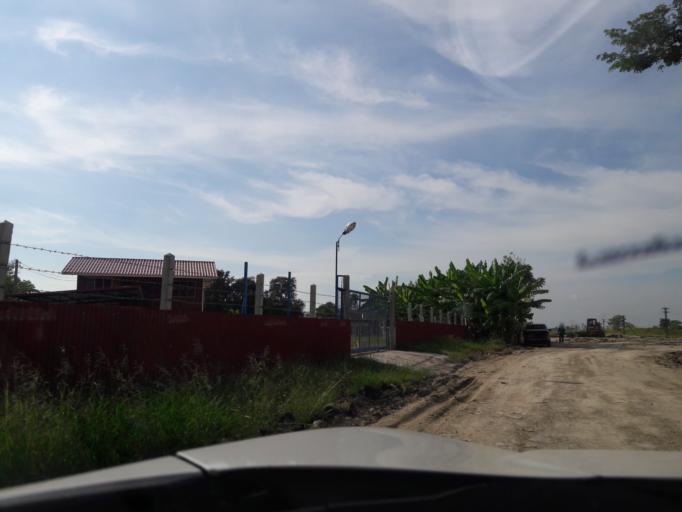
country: TH
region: Lop Buri
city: Ban Mi
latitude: 15.0479
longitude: 100.5320
